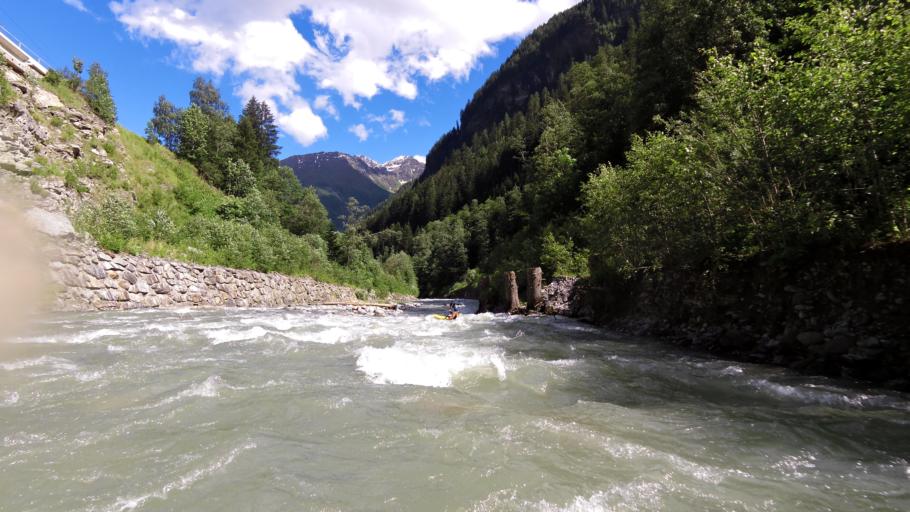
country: AT
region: Tyrol
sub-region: Politischer Bezirk Landeck
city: Strengen
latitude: 47.1239
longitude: 10.4642
